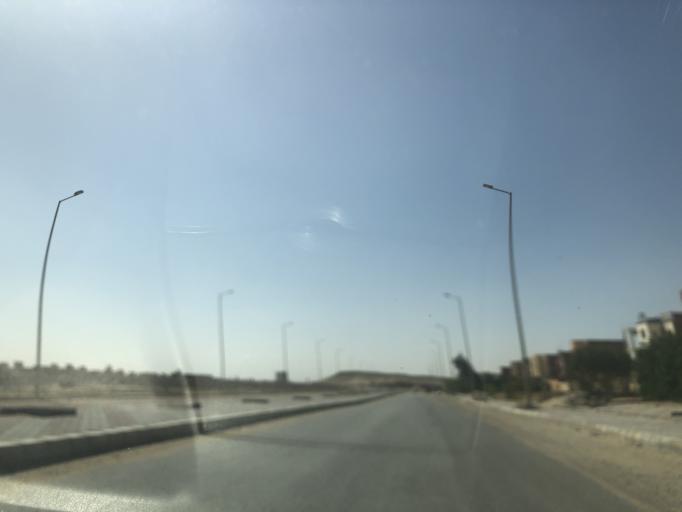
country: EG
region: Al Jizah
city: Madinat Sittah Uktubar
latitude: 29.9324
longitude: 30.9606
